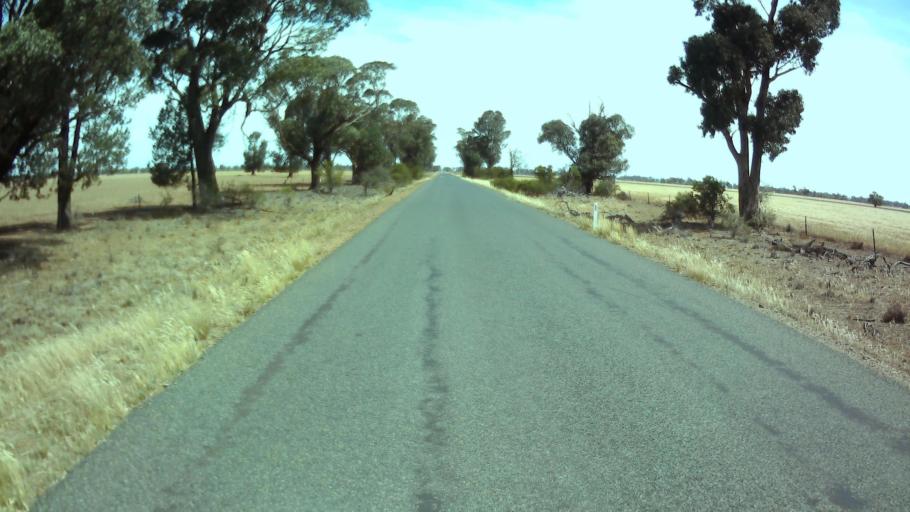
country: AU
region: New South Wales
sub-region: Weddin
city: Grenfell
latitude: -33.9788
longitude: 147.7784
